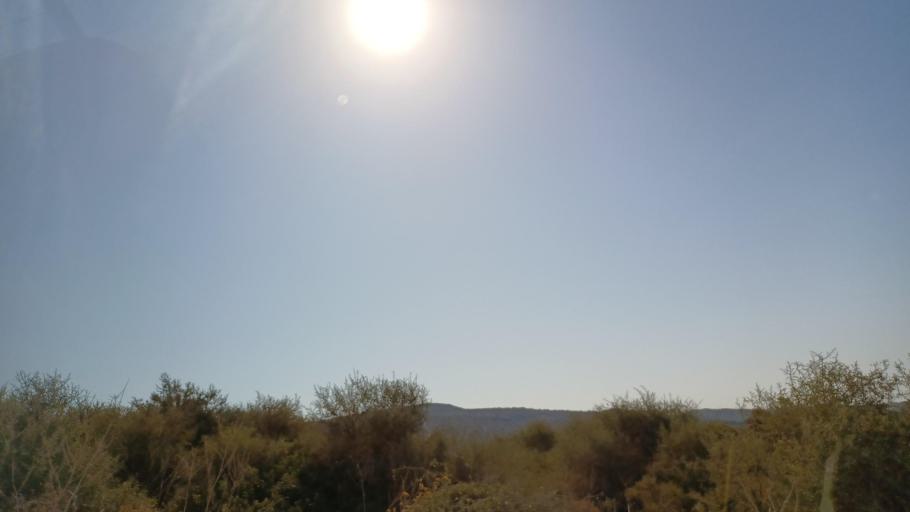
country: CY
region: Limassol
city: Pissouri
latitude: 34.7207
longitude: 32.6766
